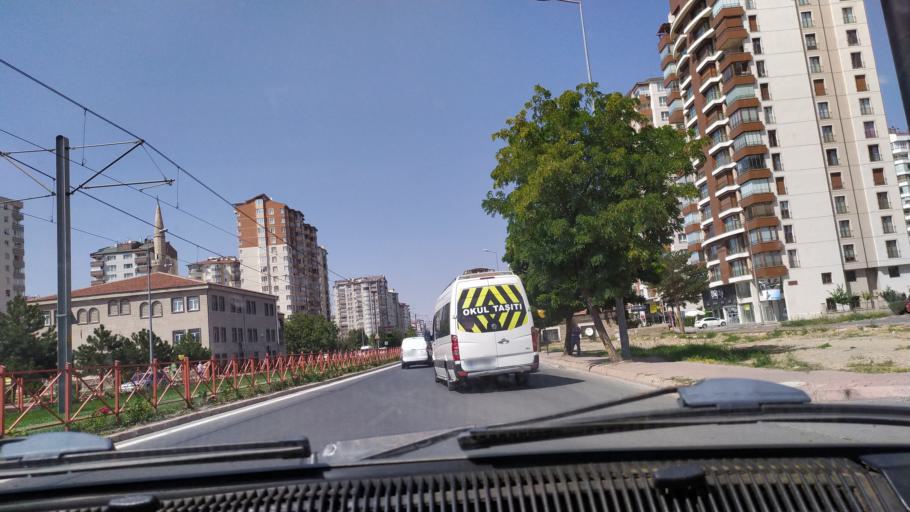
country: TR
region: Kayseri
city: Kayseri
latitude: 38.7247
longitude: 35.5271
